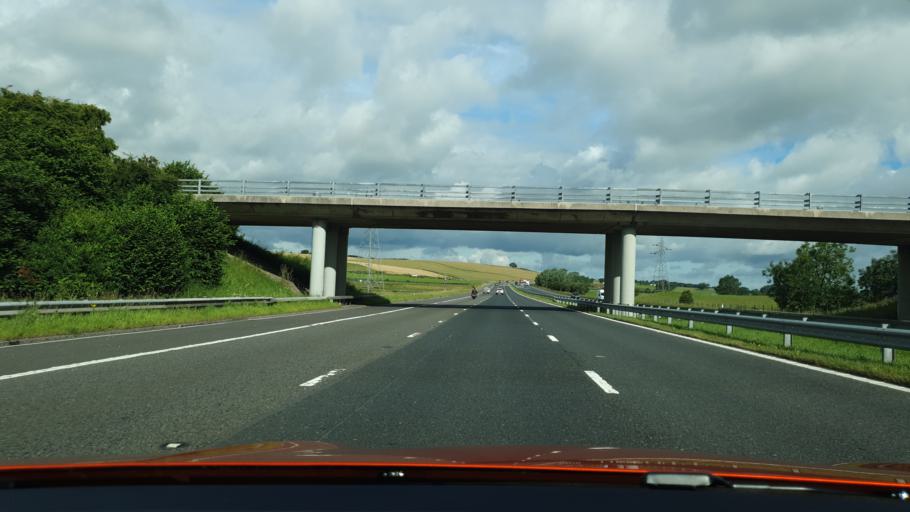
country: GB
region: England
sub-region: Cumbria
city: Penrith
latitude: 54.5597
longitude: -2.6773
